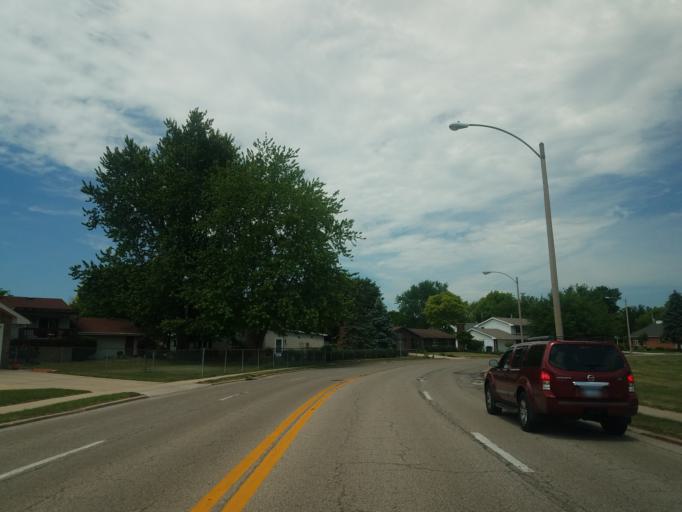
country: US
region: Illinois
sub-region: McLean County
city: Bloomington
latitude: 40.4783
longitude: -88.9586
